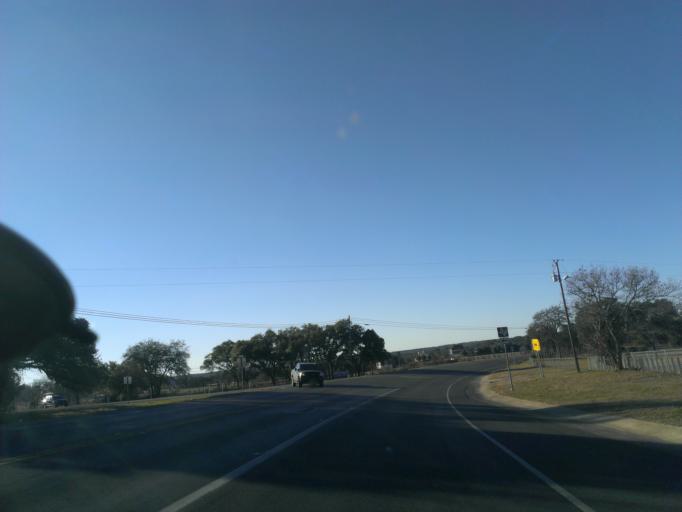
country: US
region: Texas
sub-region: Hays County
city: Dripping Springs
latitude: 30.1686
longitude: -98.0868
